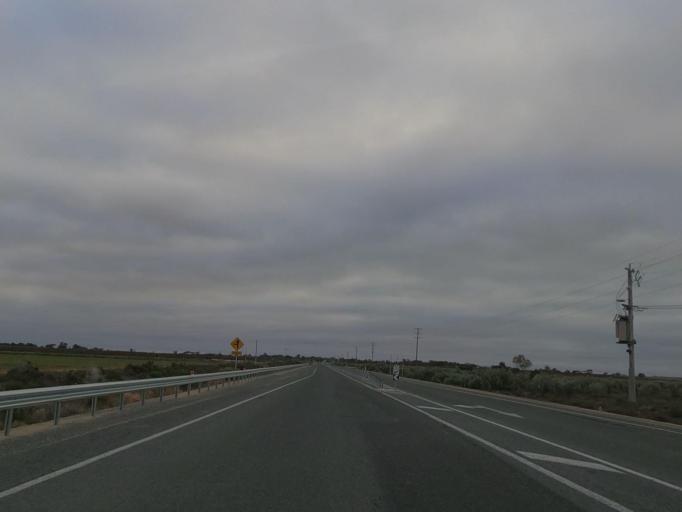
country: AU
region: Victoria
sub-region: Swan Hill
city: Swan Hill
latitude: -35.4752
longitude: 143.6781
